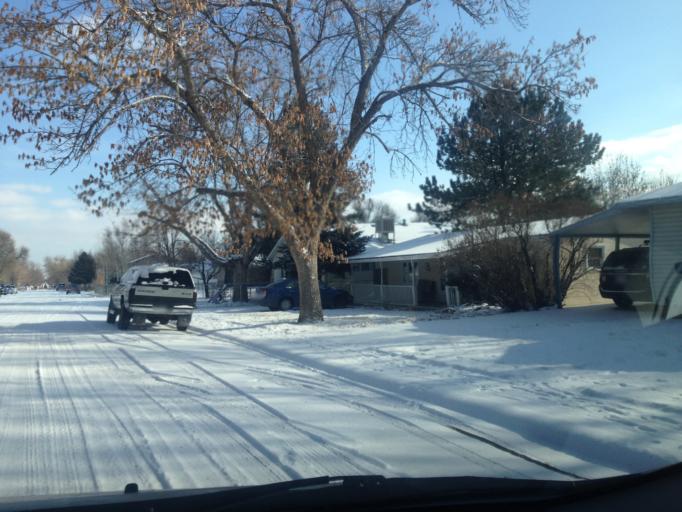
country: US
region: Colorado
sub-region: Boulder County
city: Lafayette
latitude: 39.9952
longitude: -105.0952
